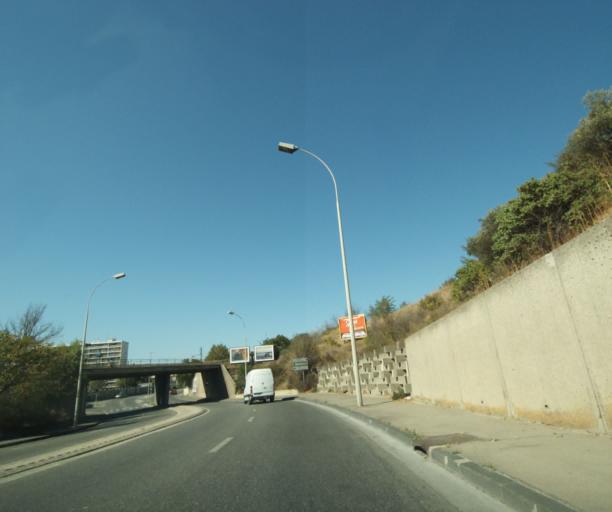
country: FR
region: Provence-Alpes-Cote d'Azur
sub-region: Departement des Bouches-du-Rhone
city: Marseille 14
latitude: 43.3400
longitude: 5.3892
